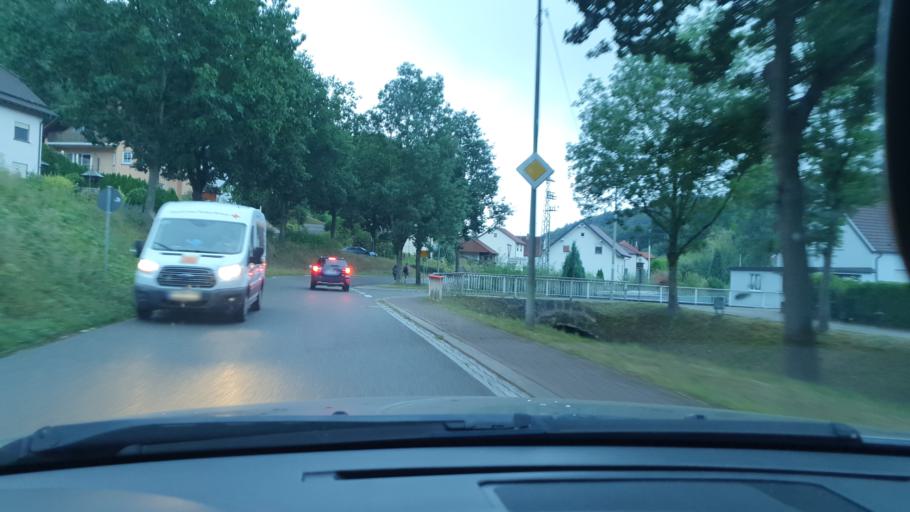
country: DE
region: Rheinland-Pfalz
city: Obernheim-Kirchenarnbach
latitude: 49.3563
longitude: 7.5759
